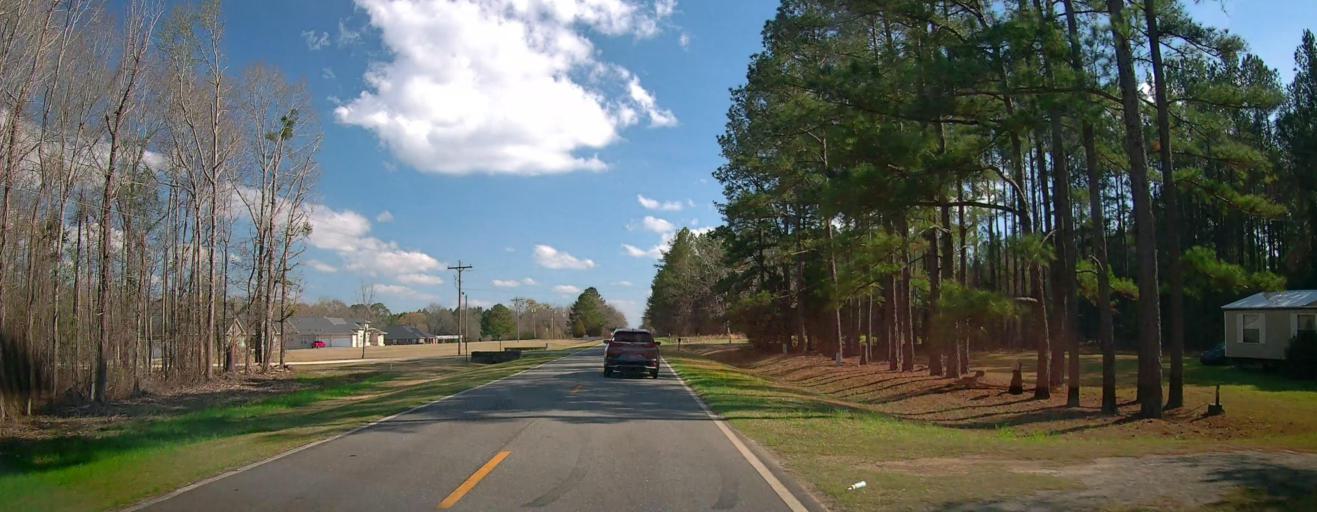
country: US
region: Georgia
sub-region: Laurens County
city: Dublin
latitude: 32.6138
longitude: -83.0829
